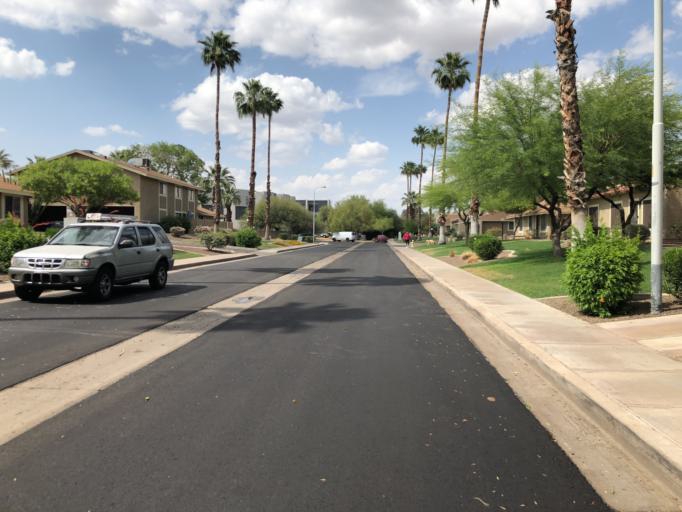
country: US
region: Arizona
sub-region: Maricopa County
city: Scottsdale
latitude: 33.4618
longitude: -111.8994
